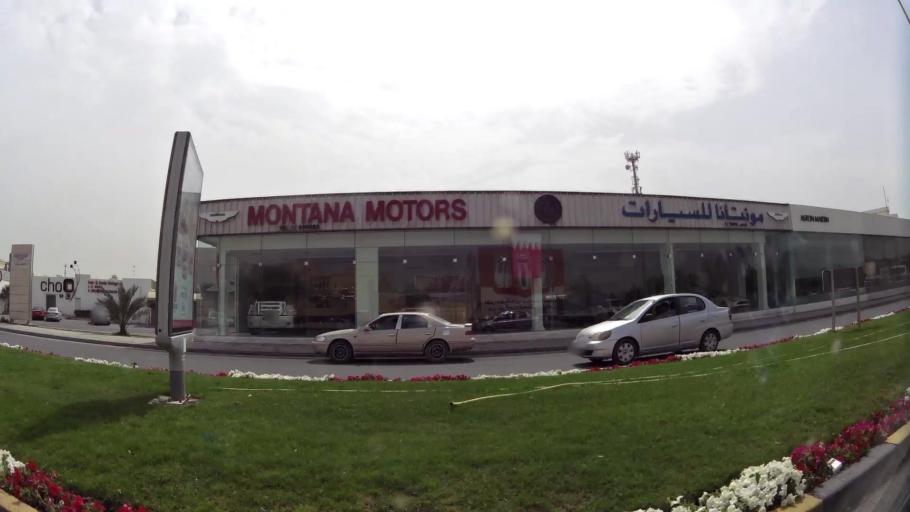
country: BH
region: Northern
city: Ar Rifa'
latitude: 26.1320
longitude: 50.5440
